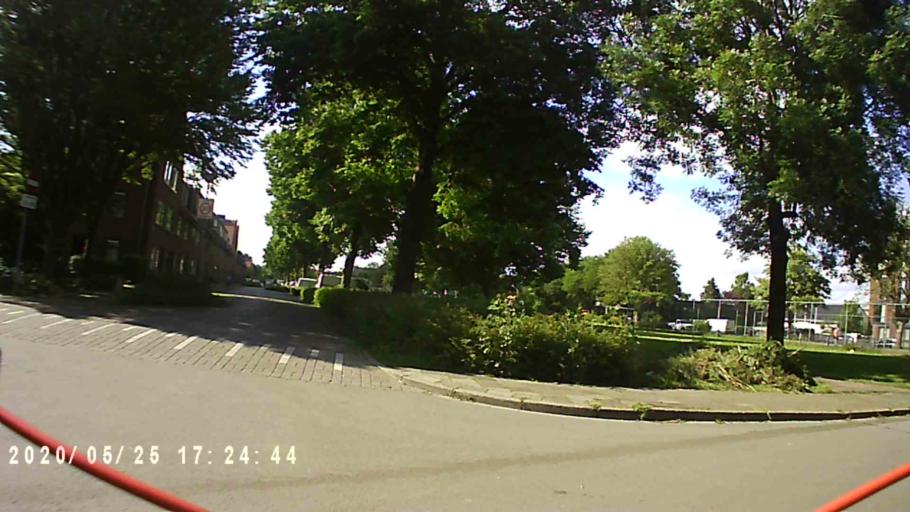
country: NL
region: Groningen
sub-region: Gemeente Groningen
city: Oosterpark
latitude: 53.2293
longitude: 6.5844
